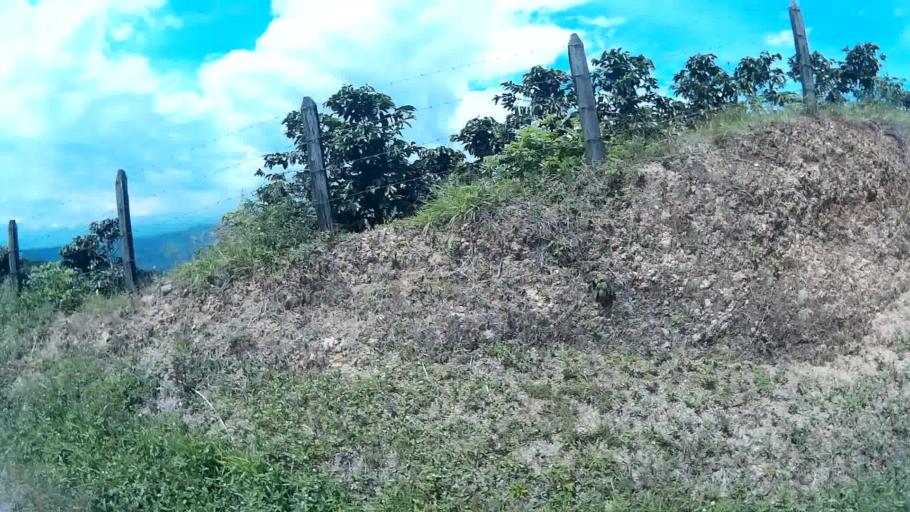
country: CO
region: Caldas
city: Belalcazar
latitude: 4.9691
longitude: -75.8216
